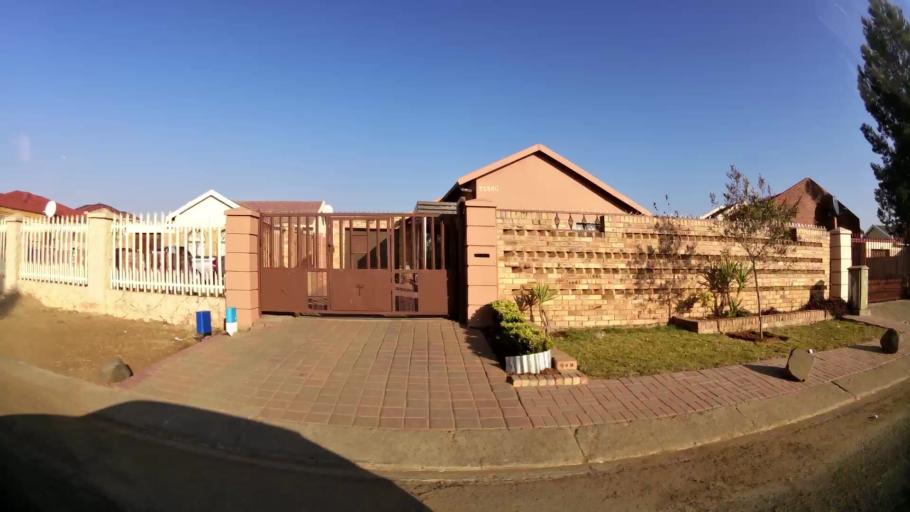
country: ZA
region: Orange Free State
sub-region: Mangaung Metropolitan Municipality
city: Bloemfontein
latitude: -29.1519
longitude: 26.2147
